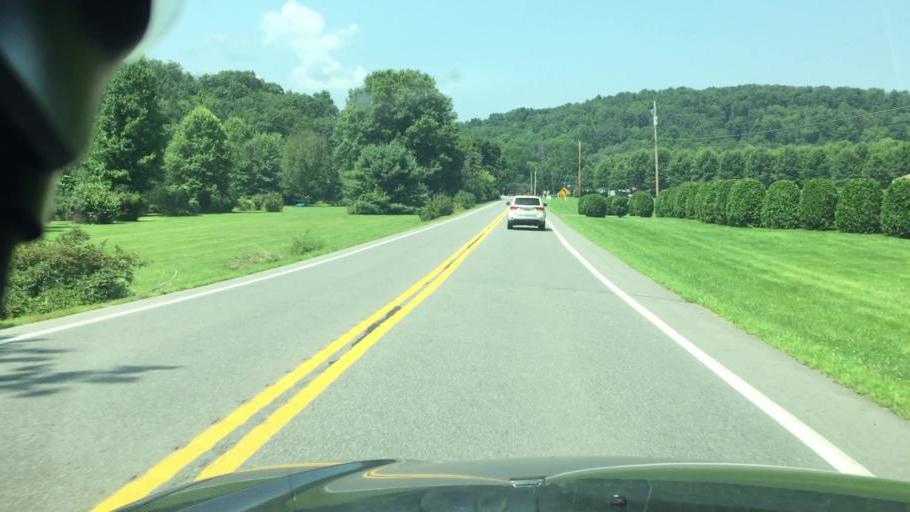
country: US
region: Pennsylvania
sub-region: Northumberland County
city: Elysburg
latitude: 40.9028
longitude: -76.5046
